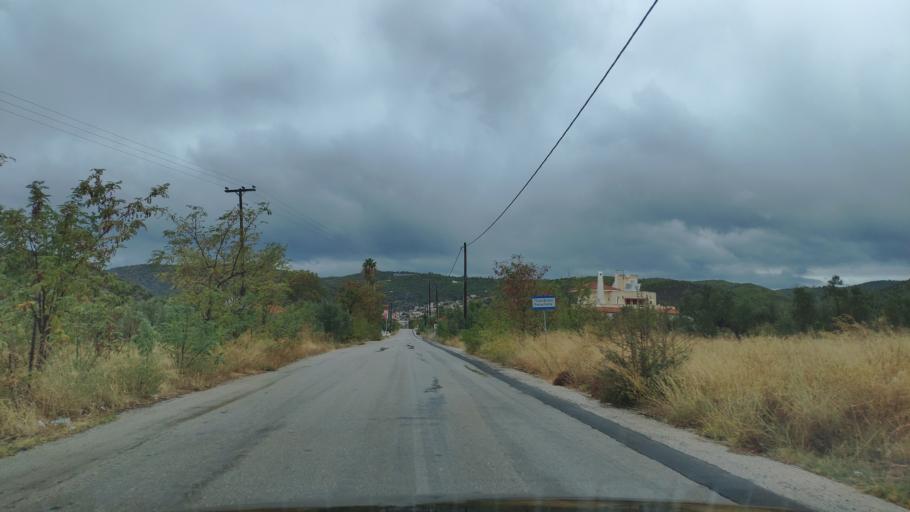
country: GR
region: Peloponnese
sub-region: Nomos Korinthias
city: Perachora
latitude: 38.0173
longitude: 22.9471
